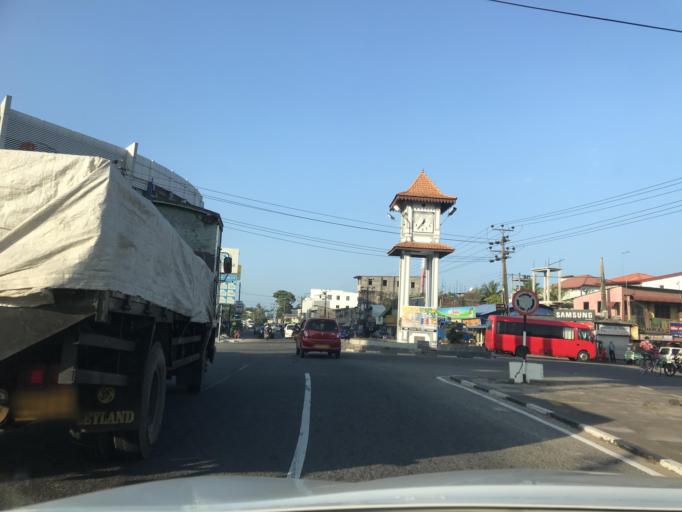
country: LK
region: Western
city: Ja Ela
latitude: 7.1011
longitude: 79.9102
